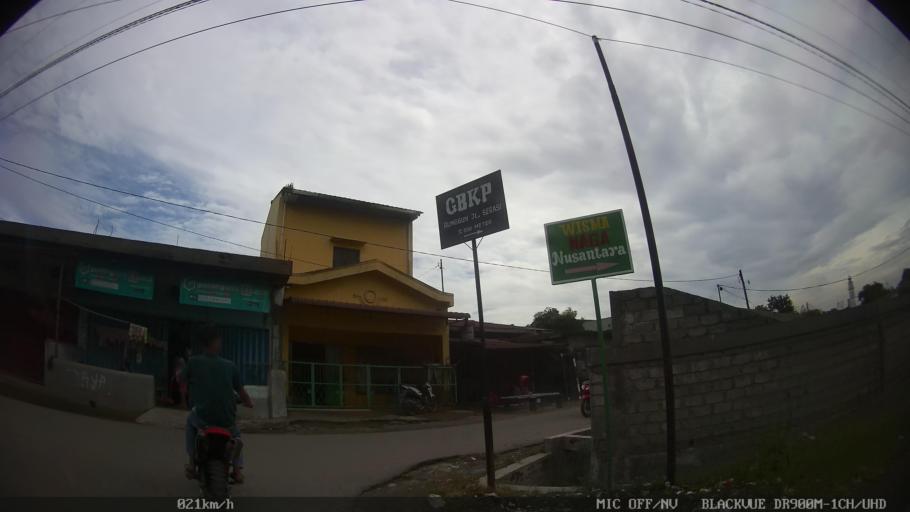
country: ID
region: North Sumatra
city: Sunggal
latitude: 3.5908
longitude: 98.5674
